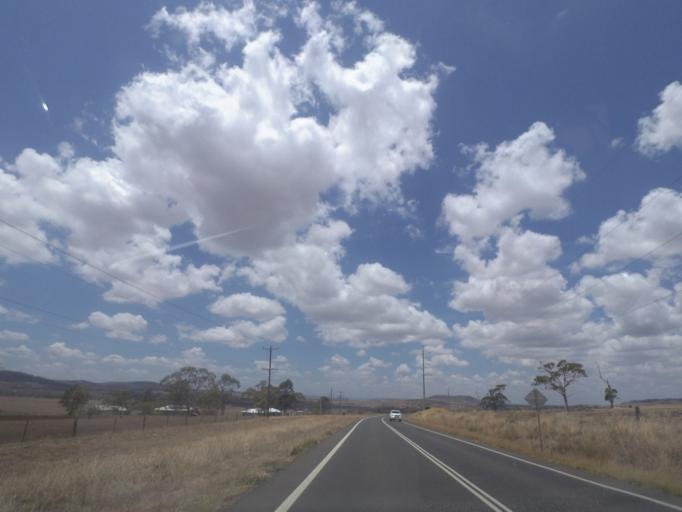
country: AU
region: Queensland
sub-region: Toowoomba
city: Top Camp
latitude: -27.7505
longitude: 151.9330
